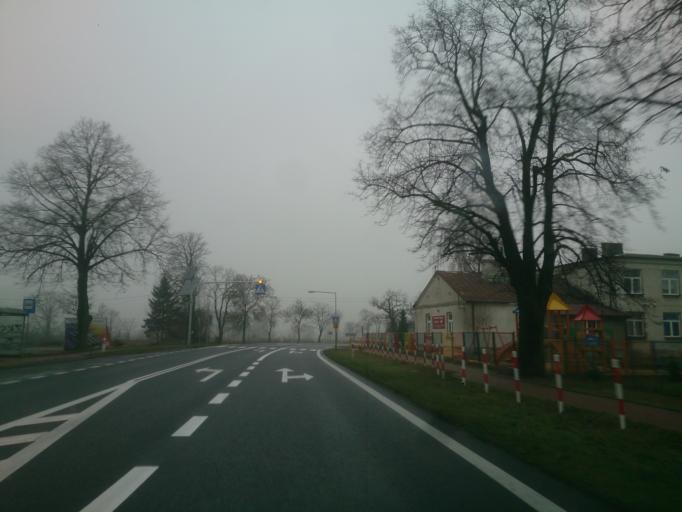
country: PL
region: Masovian Voivodeship
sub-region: Powiat sierpecki
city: Rosciszewo
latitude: 52.8180
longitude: 19.7828
